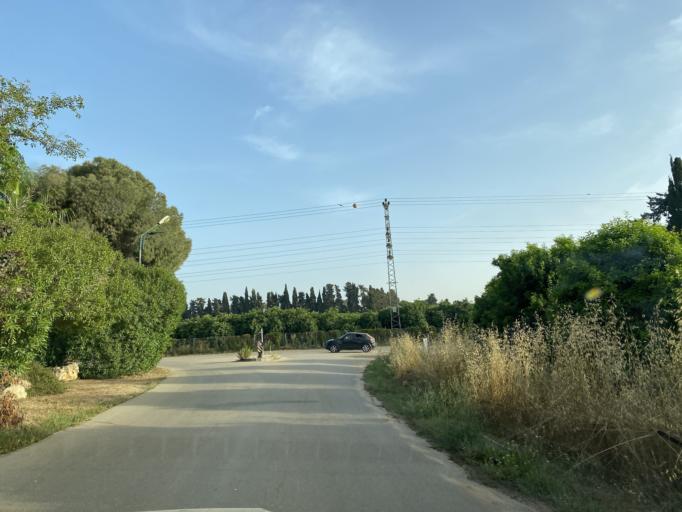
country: IL
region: Tel Aviv
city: Herzliyya
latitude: 32.1552
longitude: 34.8287
